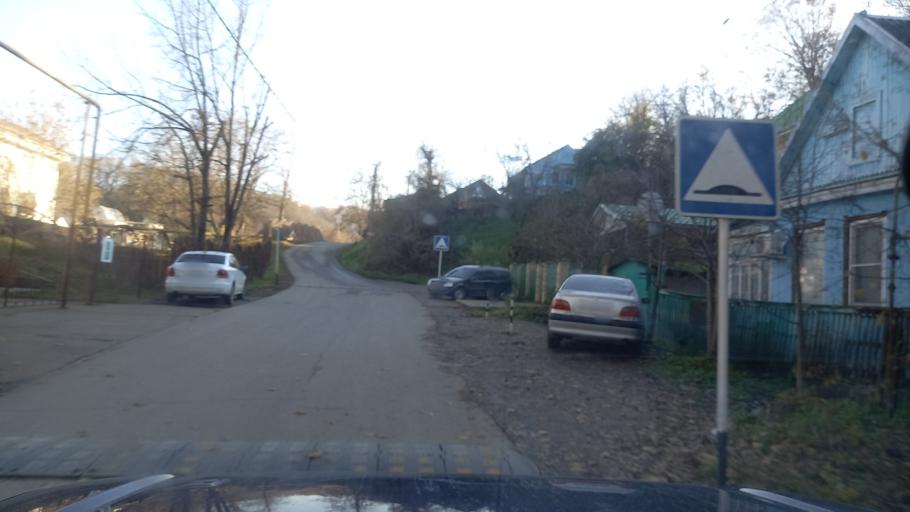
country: RU
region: Krasnodarskiy
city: Goryachiy Klyuch
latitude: 44.6256
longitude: 39.1058
